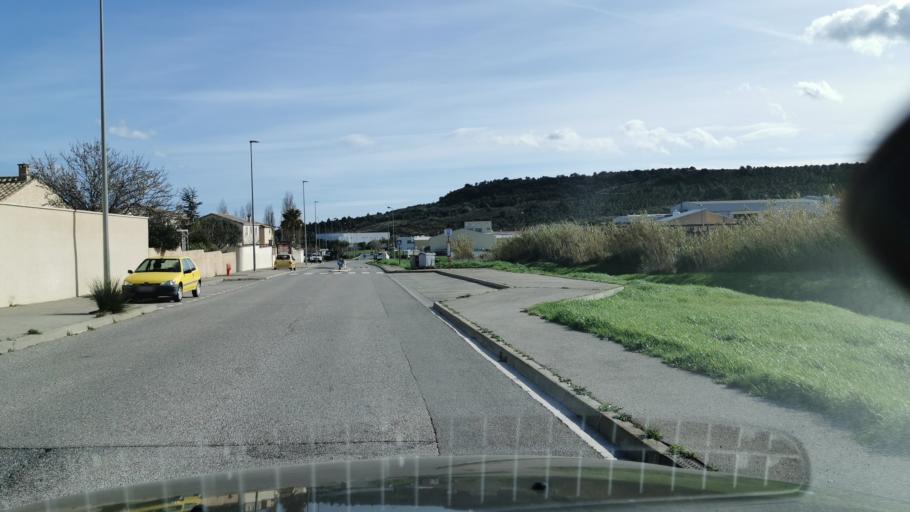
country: FR
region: Languedoc-Roussillon
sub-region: Departement de l'Aude
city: Narbonne
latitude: 43.1605
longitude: 2.9689
